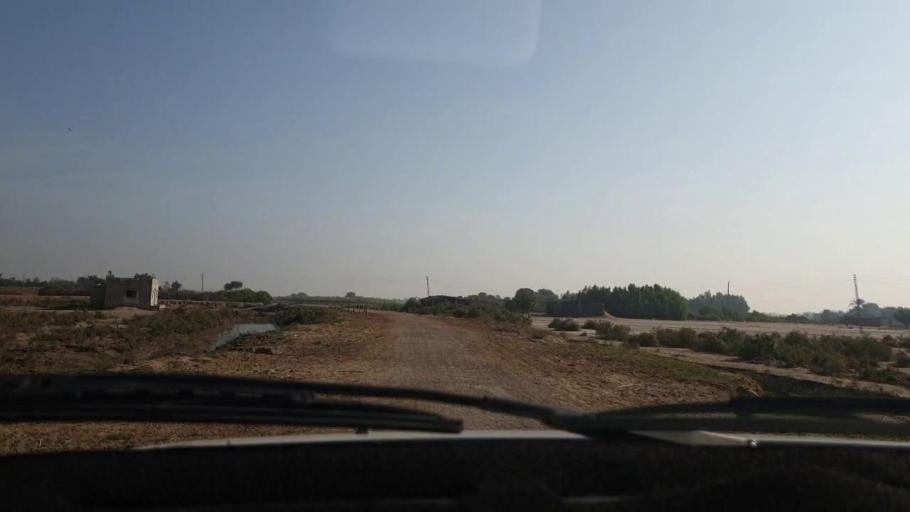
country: PK
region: Sindh
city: Tando Muhammad Khan
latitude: 25.0235
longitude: 68.4851
